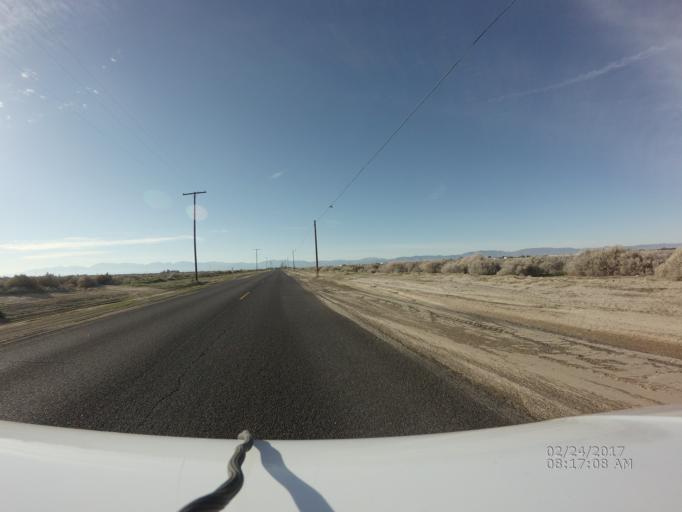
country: US
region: California
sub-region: Los Angeles County
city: Lancaster
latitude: 34.7230
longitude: -118.0412
